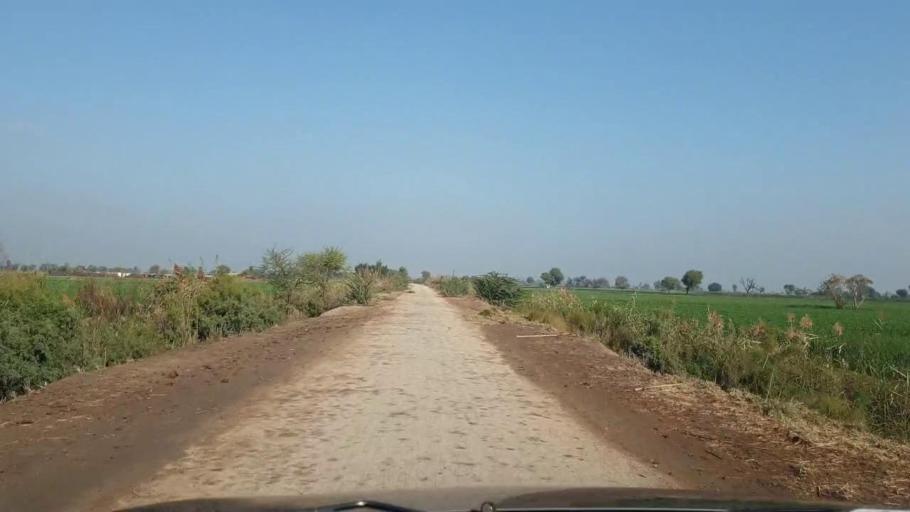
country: PK
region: Sindh
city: Sinjhoro
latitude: 26.0594
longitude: 68.7881
